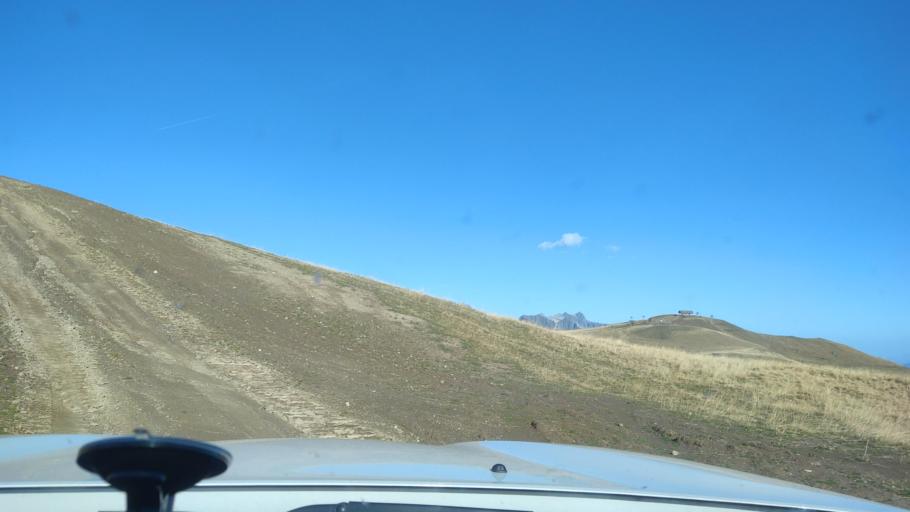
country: FR
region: Rhone-Alpes
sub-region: Departement de la Savoie
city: Saint-Etienne-de-Cuines
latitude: 45.2409
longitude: 6.2238
